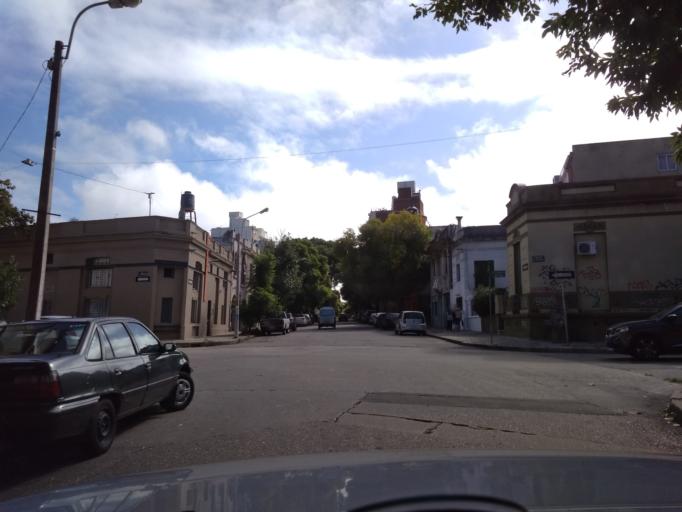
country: UY
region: Montevideo
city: Montevideo
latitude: -34.9064
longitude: -56.1581
